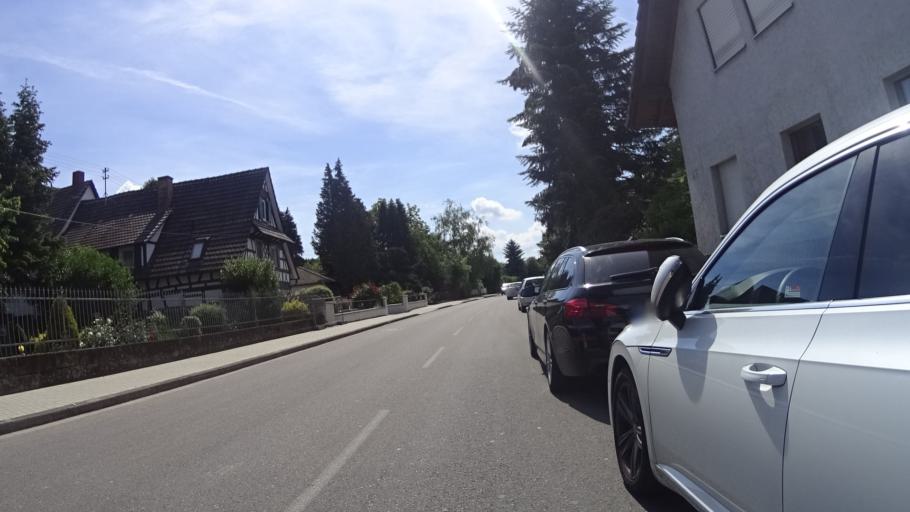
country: DE
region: Baden-Wuerttemberg
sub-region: Freiburg Region
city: Meissenheim
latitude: 48.4628
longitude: 7.8132
